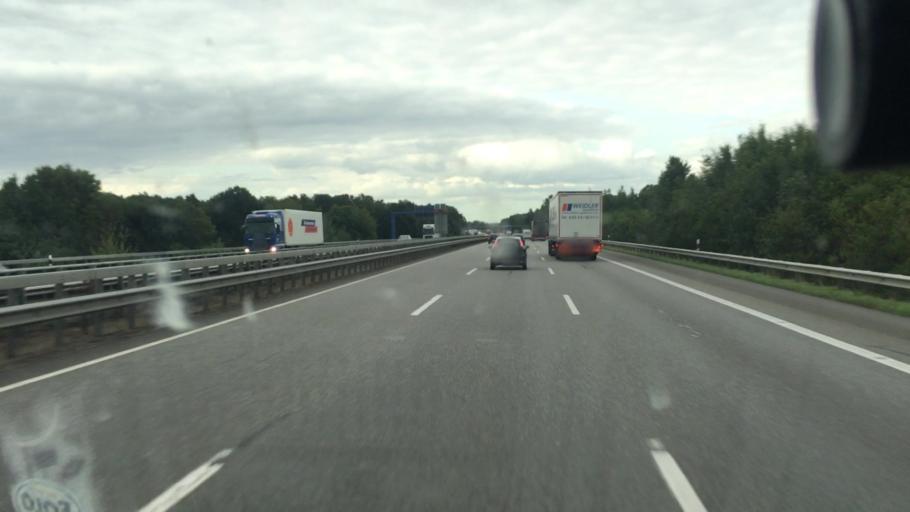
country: DE
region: Lower Saxony
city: Dinklage
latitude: 52.6680
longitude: 8.1683
